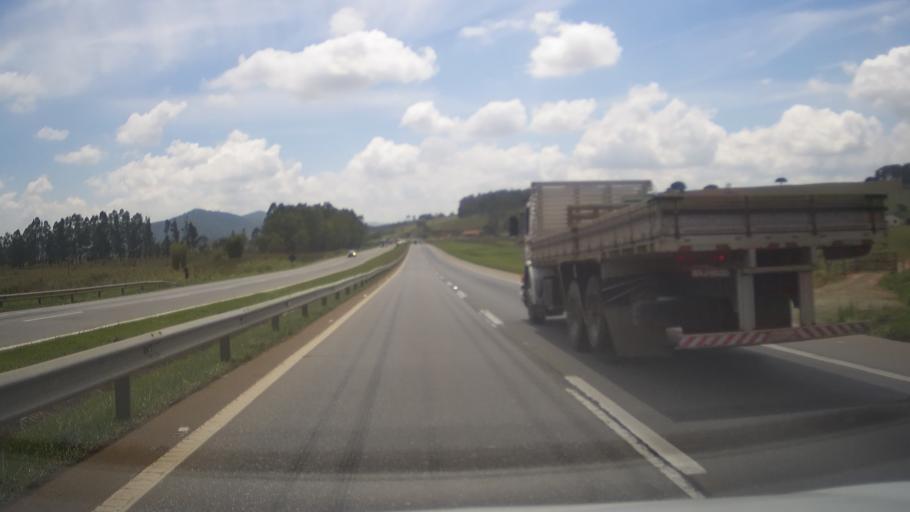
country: BR
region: Minas Gerais
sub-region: Santa Rita Do Sapucai
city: Santa Rita do Sapucai
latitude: -22.0981
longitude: -45.7184
